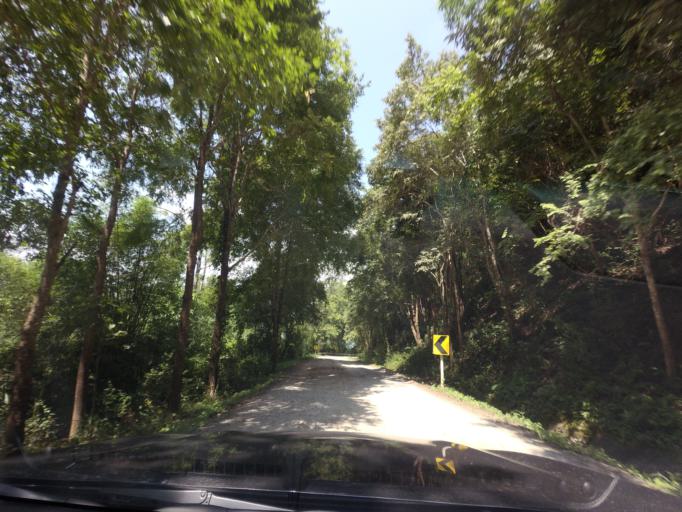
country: TH
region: Loei
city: Na Haeo
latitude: 17.6218
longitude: 100.8998
